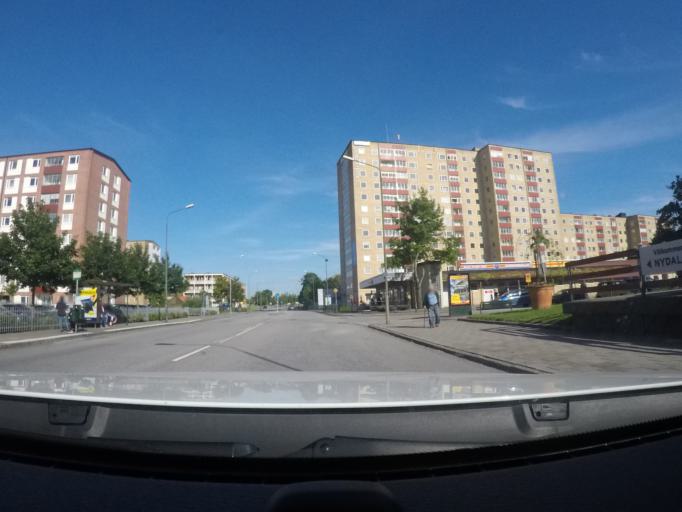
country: SE
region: Skane
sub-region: Malmo
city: Malmoe
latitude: 55.5744
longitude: 13.0197
